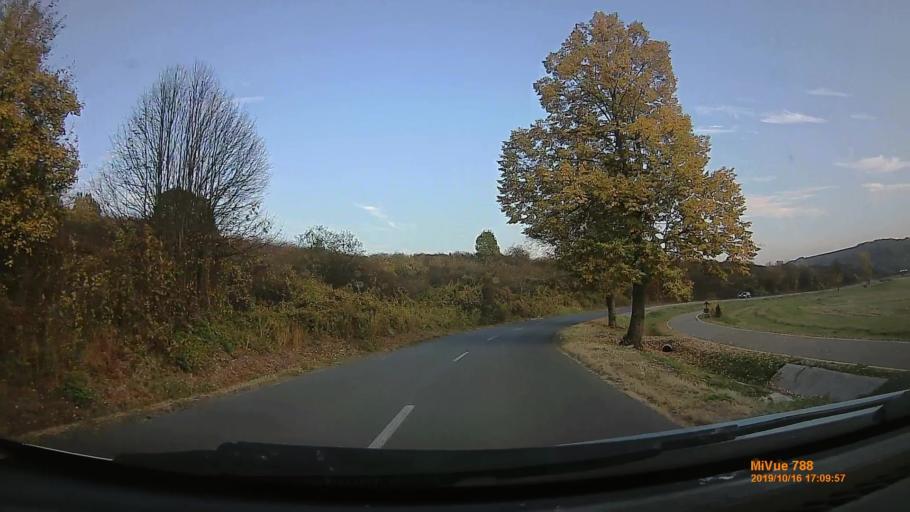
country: HU
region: Heves
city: Egerszalok
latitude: 47.8463
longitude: 20.3309
